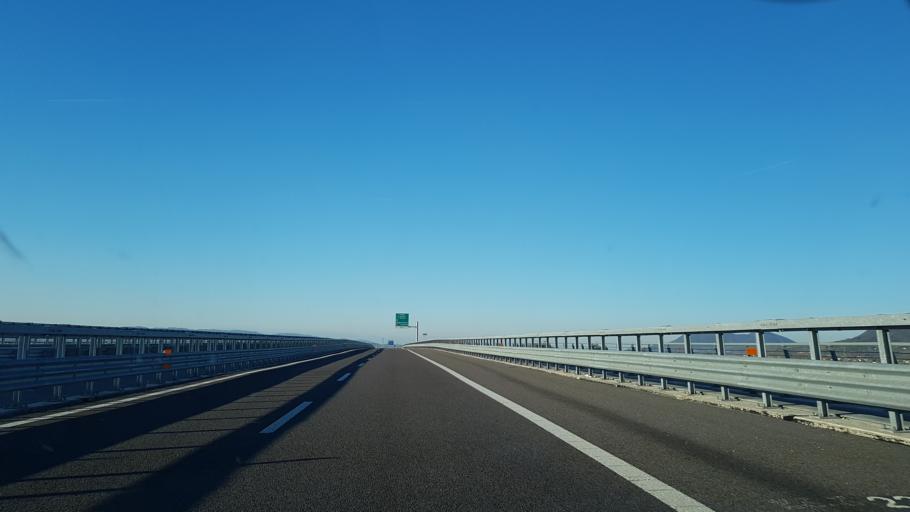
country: IT
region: Veneto
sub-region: Provincia di Vicenza
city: Noventa Vicentina
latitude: 45.2594
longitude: 11.5706
